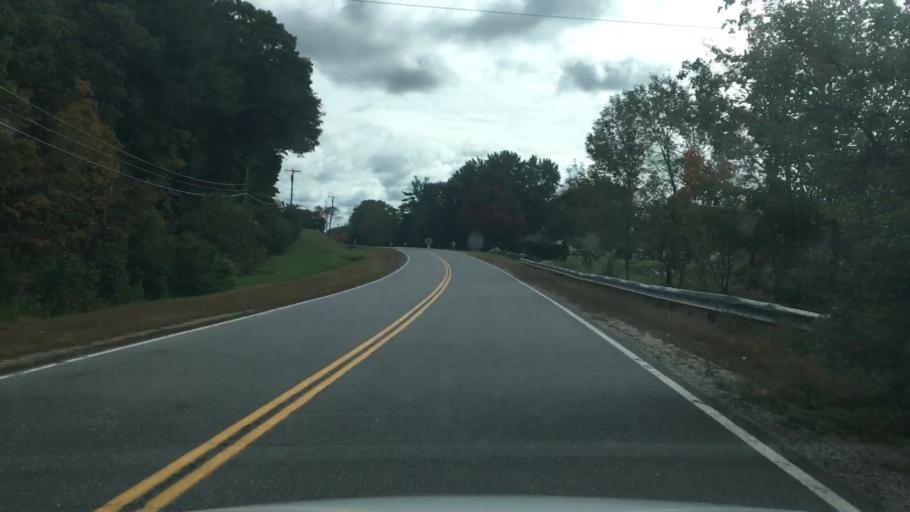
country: US
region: Maine
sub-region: Androscoggin County
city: Lewiston
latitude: 44.0570
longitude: -70.2053
